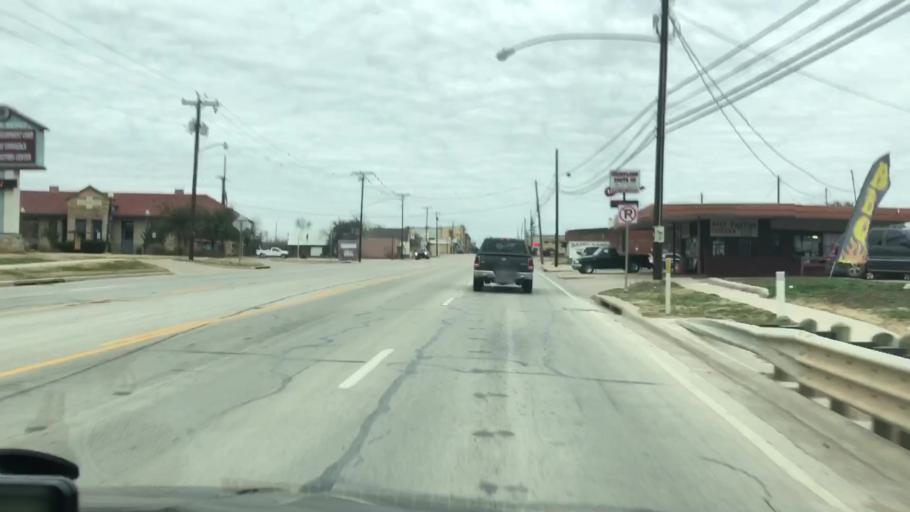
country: US
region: Texas
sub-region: Jack County
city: Jacksboro
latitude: 33.2144
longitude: -98.1588
